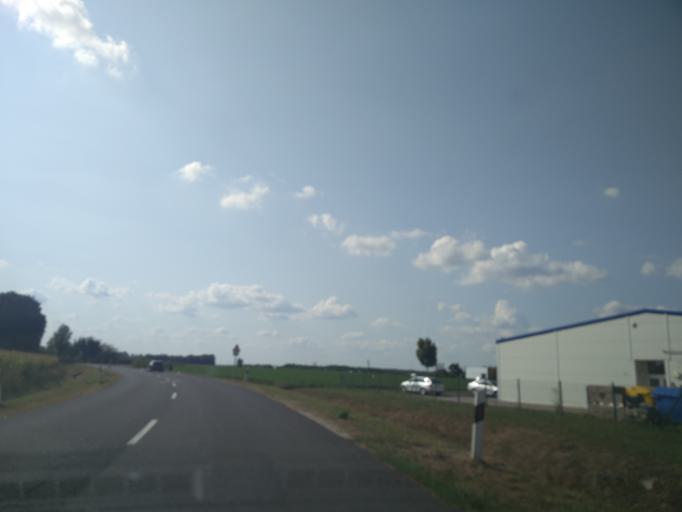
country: HU
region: Zala
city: Zalaegerszeg
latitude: 46.8802
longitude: 16.8285
